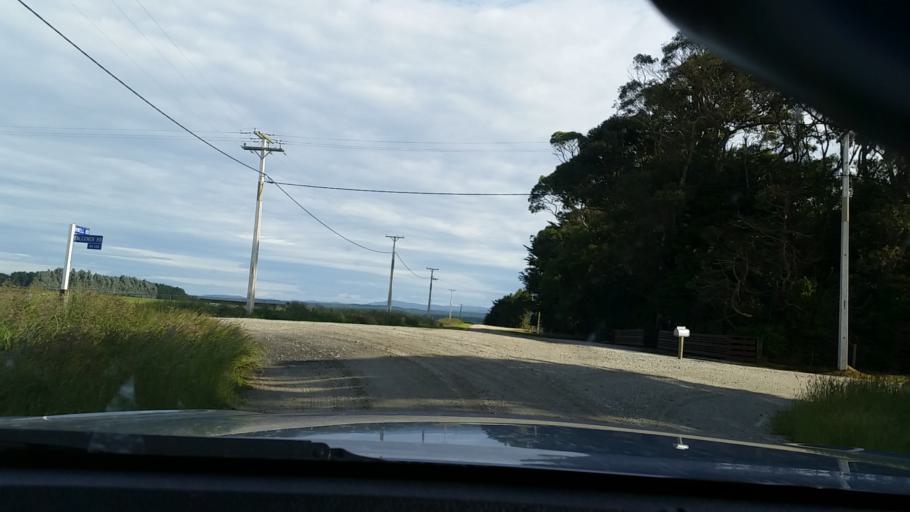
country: NZ
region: Southland
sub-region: Invercargill City
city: Invercargill
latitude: -46.2851
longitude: 168.6229
